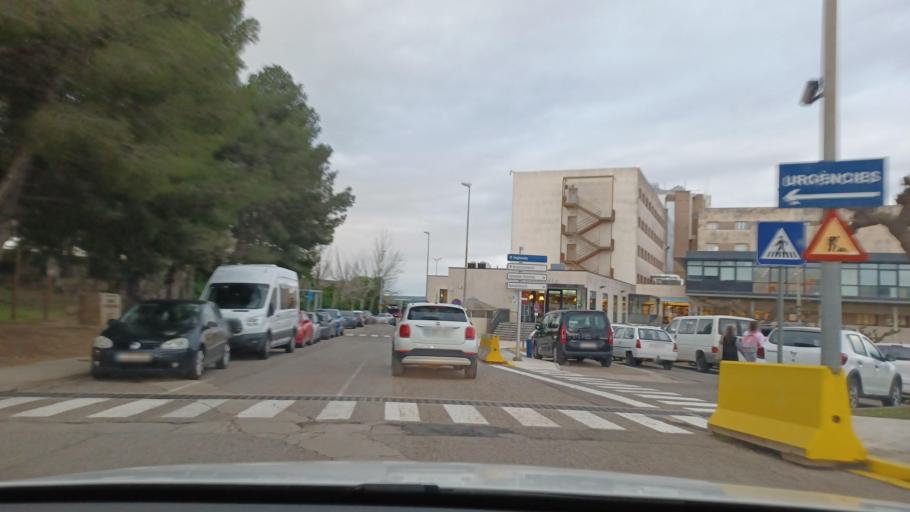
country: ES
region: Catalonia
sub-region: Provincia de Tarragona
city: Tortosa
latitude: 40.8118
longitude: 0.5255
